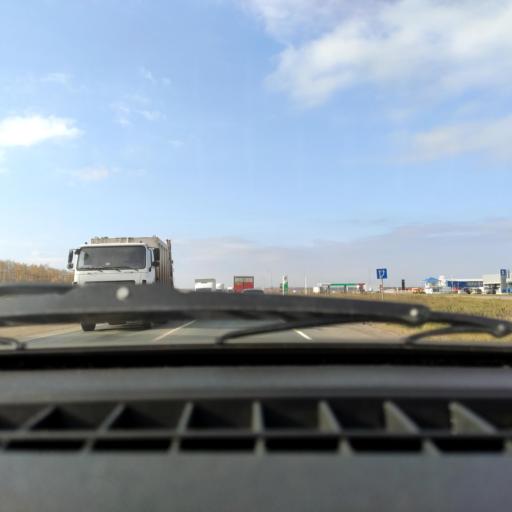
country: RU
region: Bashkortostan
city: Iglino
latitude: 54.7398
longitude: 56.2934
